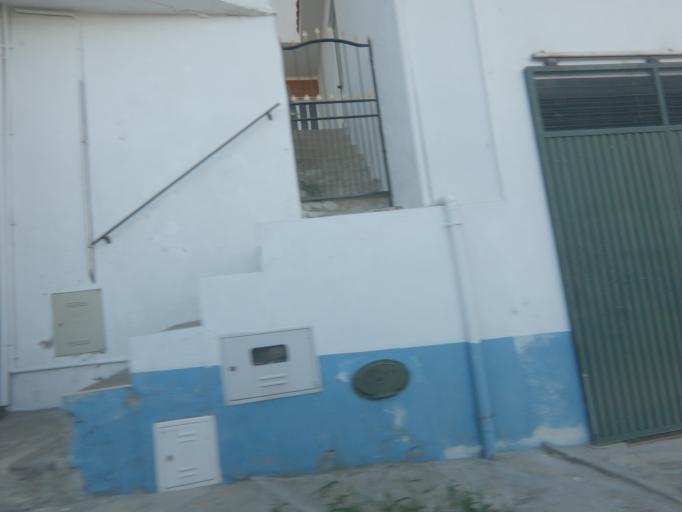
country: PT
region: Vila Real
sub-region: Peso da Regua
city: Godim
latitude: 41.1640
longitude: -7.8101
